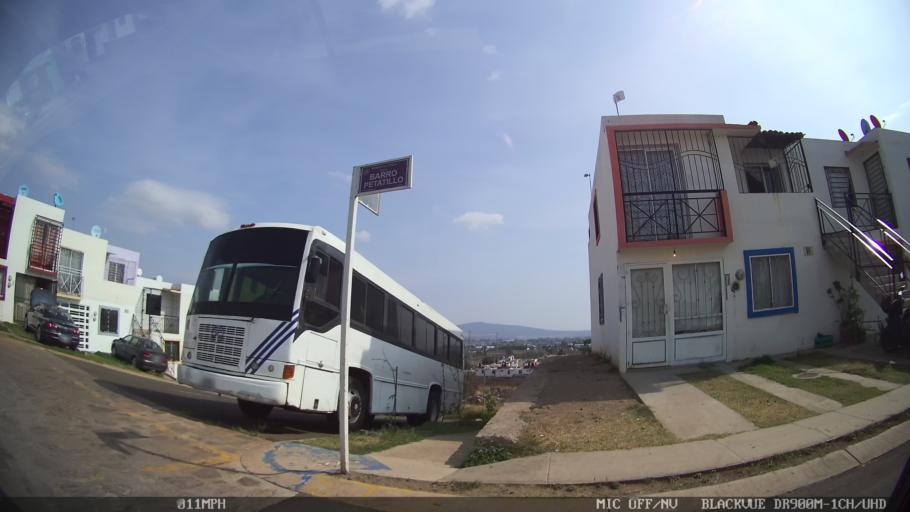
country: MX
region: Jalisco
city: Tonala
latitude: 20.6410
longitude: -103.2346
